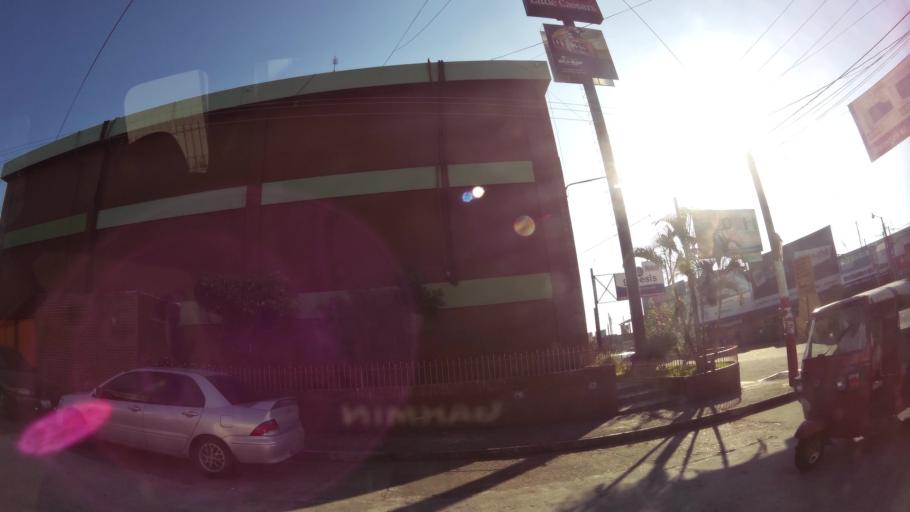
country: GT
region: Suchitepeque
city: Mazatenango
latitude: 14.5340
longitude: -91.5085
